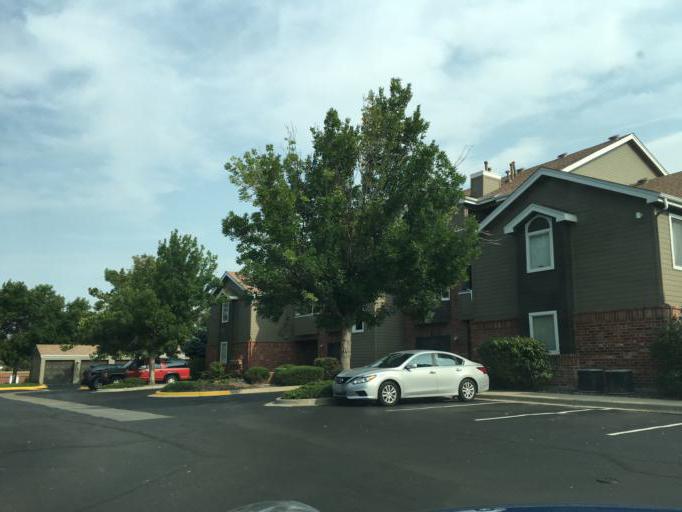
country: US
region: Colorado
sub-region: Arapahoe County
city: Glendale
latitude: 39.7070
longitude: -104.9305
